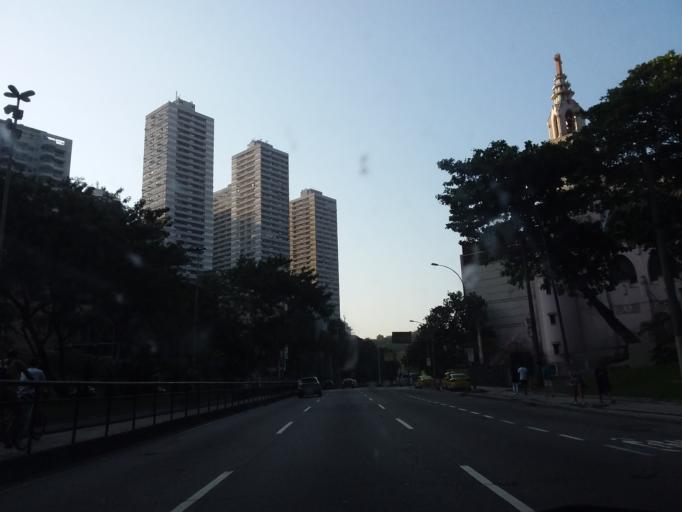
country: BR
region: Rio de Janeiro
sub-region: Rio De Janeiro
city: Rio de Janeiro
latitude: -22.9592
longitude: -43.1764
